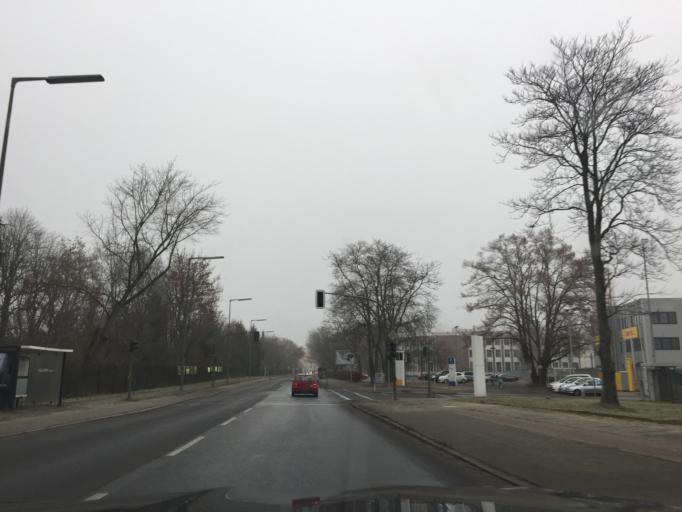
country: DE
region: Berlin
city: Siemensstadt
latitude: 52.5309
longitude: 13.2675
